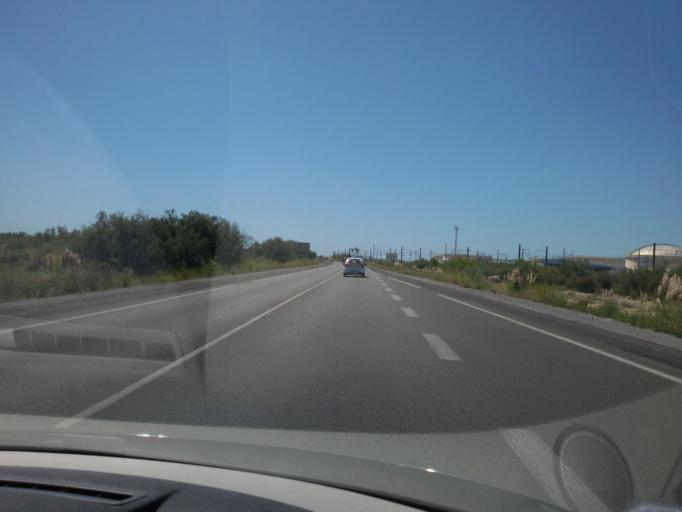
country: FR
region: Languedoc-Roussillon
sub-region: Departement de l'Herault
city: Frontignan
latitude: 43.4351
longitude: 3.7585
